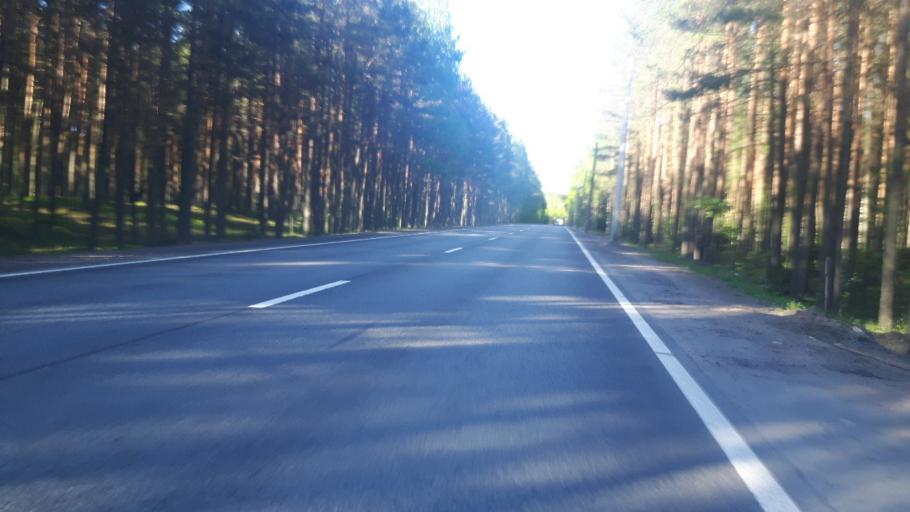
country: RU
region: Leningrad
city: Molodezhnoye
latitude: 60.1771
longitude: 29.4447
